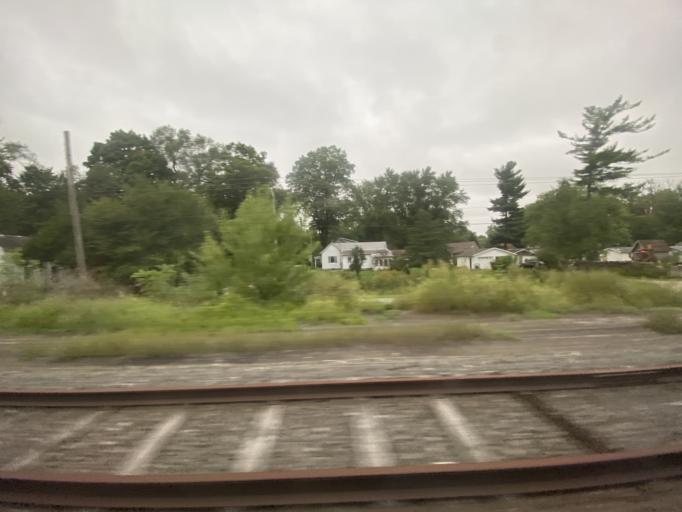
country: US
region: Indiana
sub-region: LaPorte County
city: Westville
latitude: 41.5989
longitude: -86.9099
